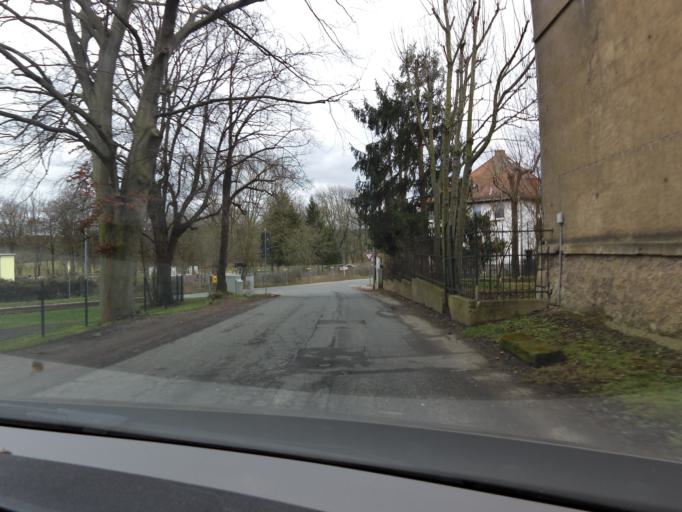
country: DE
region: Thuringia
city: Apolda
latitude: 51.0162
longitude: 11.5012
